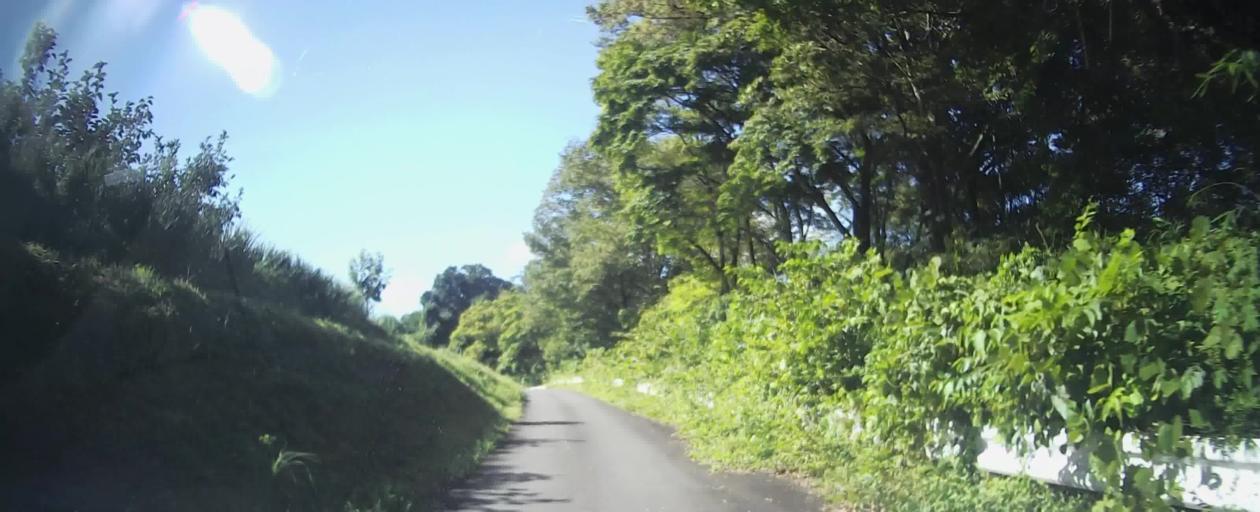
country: JP
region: Gunma
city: Nakanojomachi
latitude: 36.5677
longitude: 138.7427
